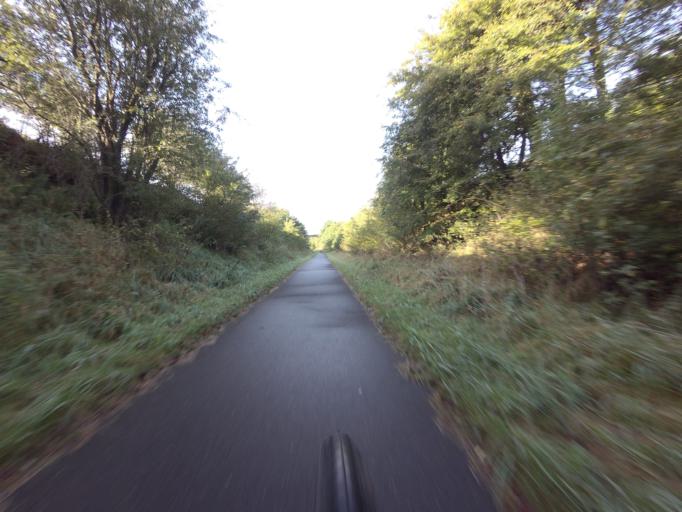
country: DK
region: Central Jutland
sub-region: Viborg Kommune
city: Bjerringbro
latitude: 56.4713
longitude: 9.5938
